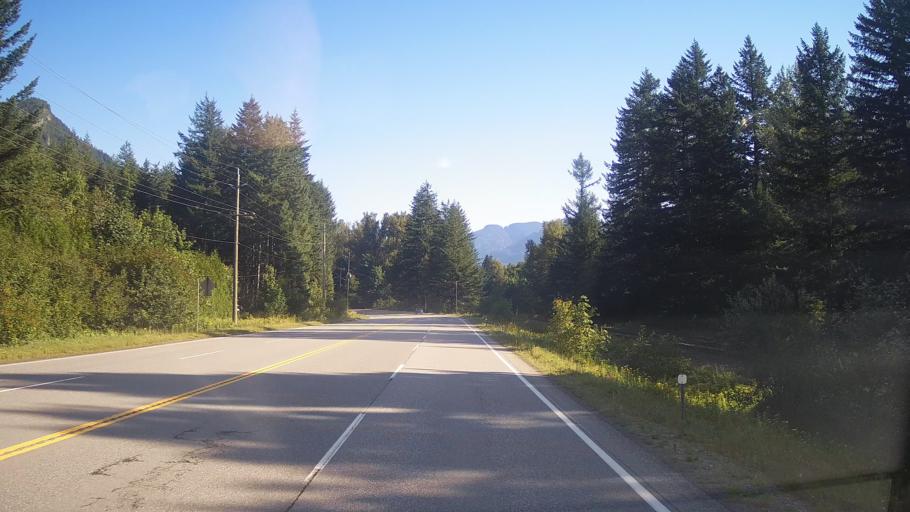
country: CA
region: British Columbia
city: Hope
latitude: 49.4399
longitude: -121.4369
